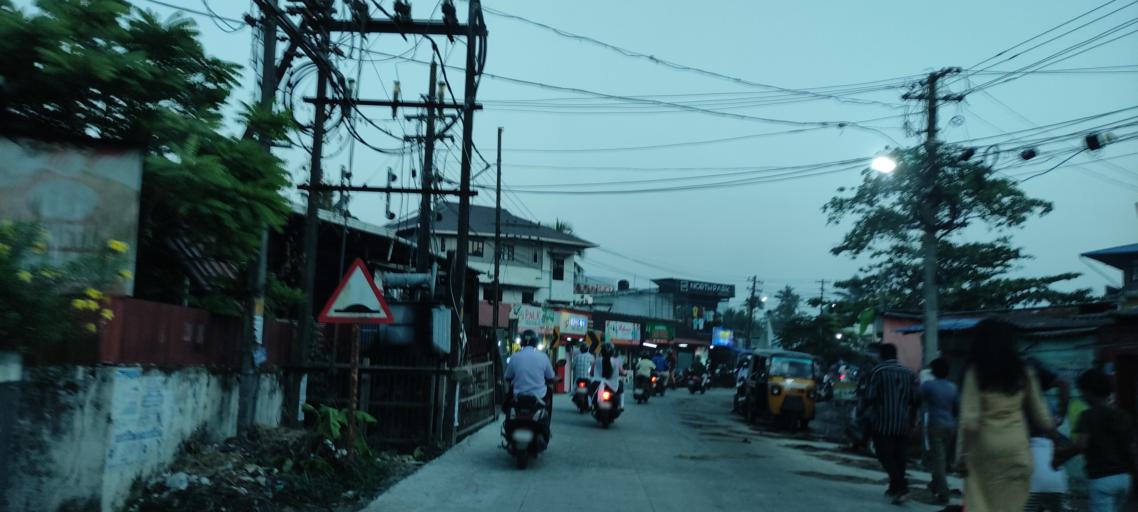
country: IN
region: Kerala
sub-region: Alappuzha
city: Alleppey
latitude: 9.5146
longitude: 76.3376
